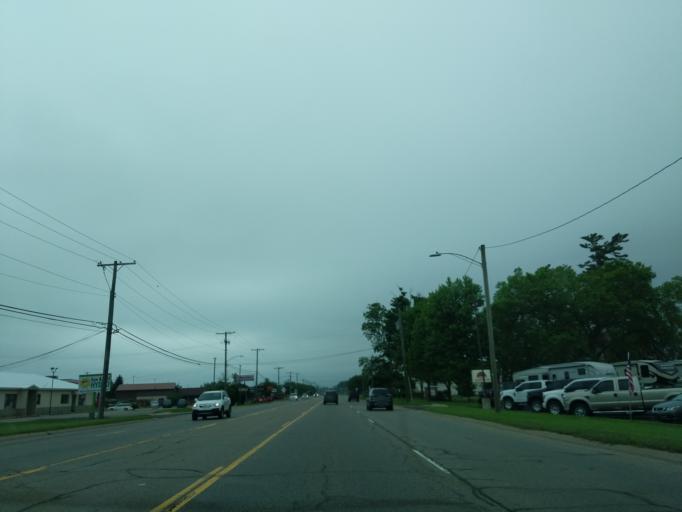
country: US
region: Michigan
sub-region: Branch County
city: Coldwater
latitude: 41.9345
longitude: -84.9630
